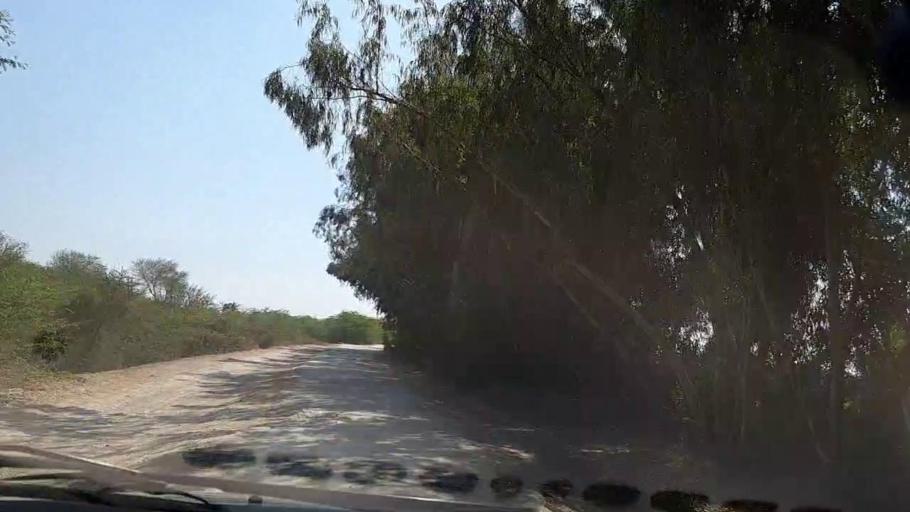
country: PK
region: Sindh
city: Mirpur Khas
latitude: 25.4800
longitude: 69.0466
